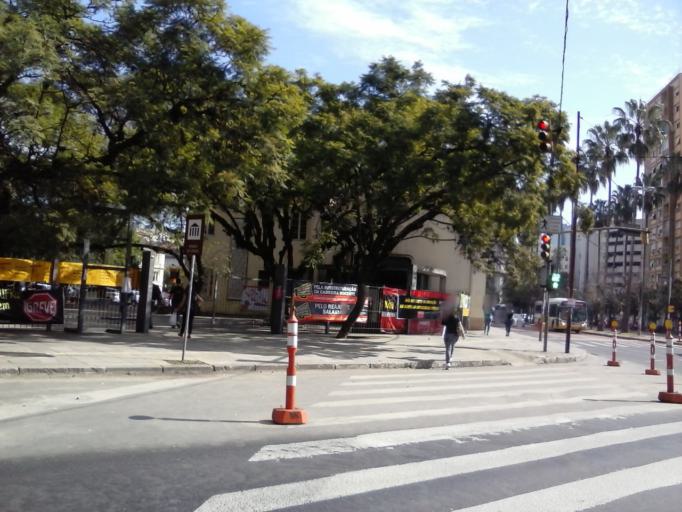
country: BR
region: Rio Grande do Sul
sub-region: Porto Alegre
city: Porto Alegre
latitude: -30.0328
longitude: -51.2191
